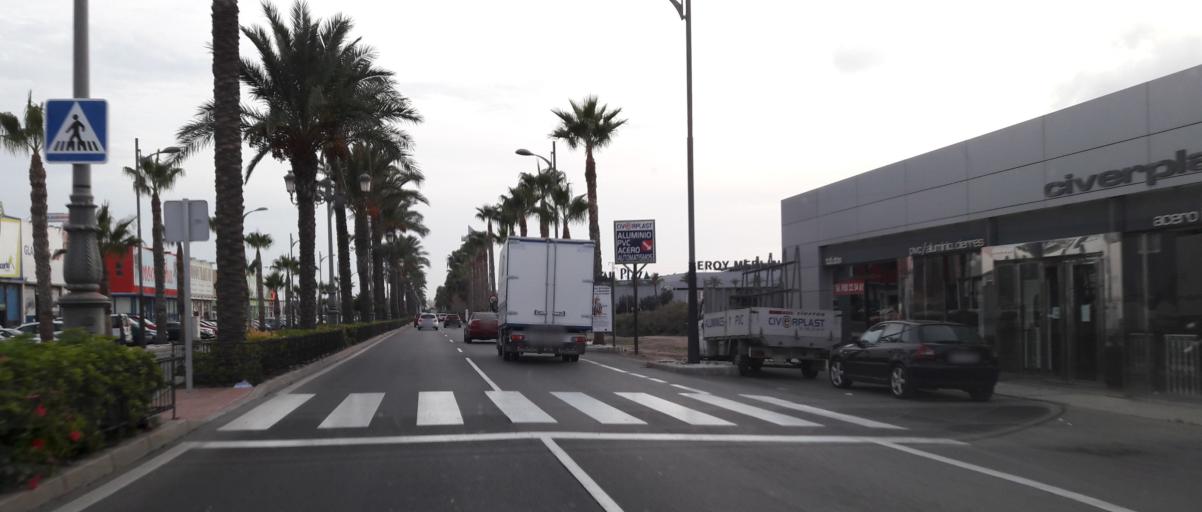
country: ES
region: Andalusia
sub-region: Provincia de Almeria
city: Roquetas de Mar
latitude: 36.7783
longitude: -2.6100
